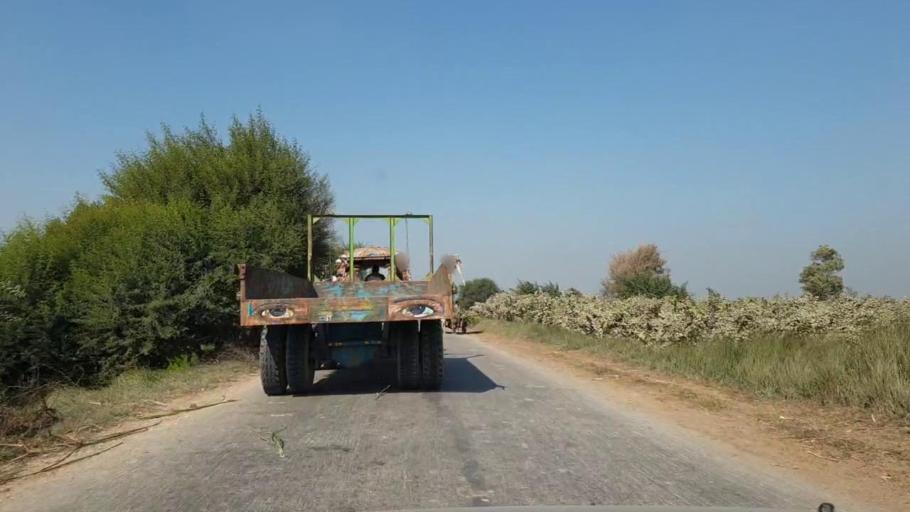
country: PK
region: Sindh
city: Tando Adam
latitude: 25.6588
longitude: 68.5852
